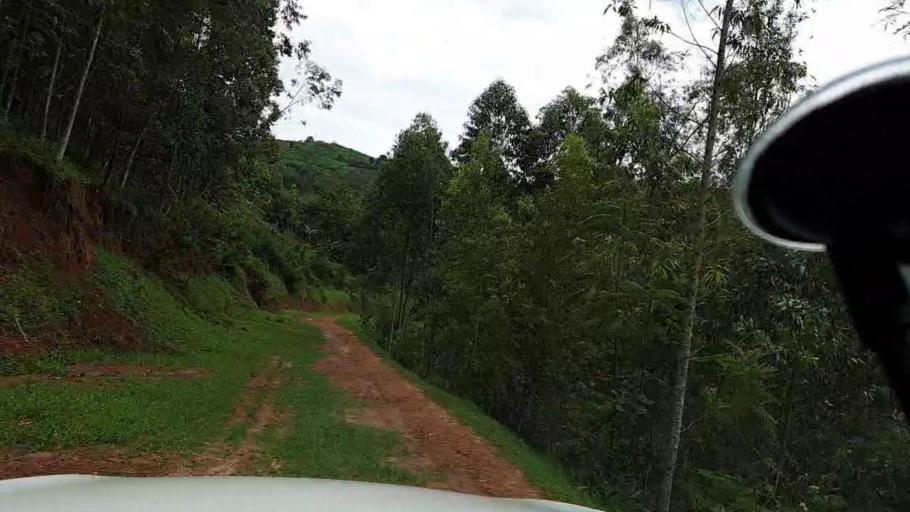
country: RW
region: Southern Province
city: Gitarama
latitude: -2.0682
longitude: 29.6448
